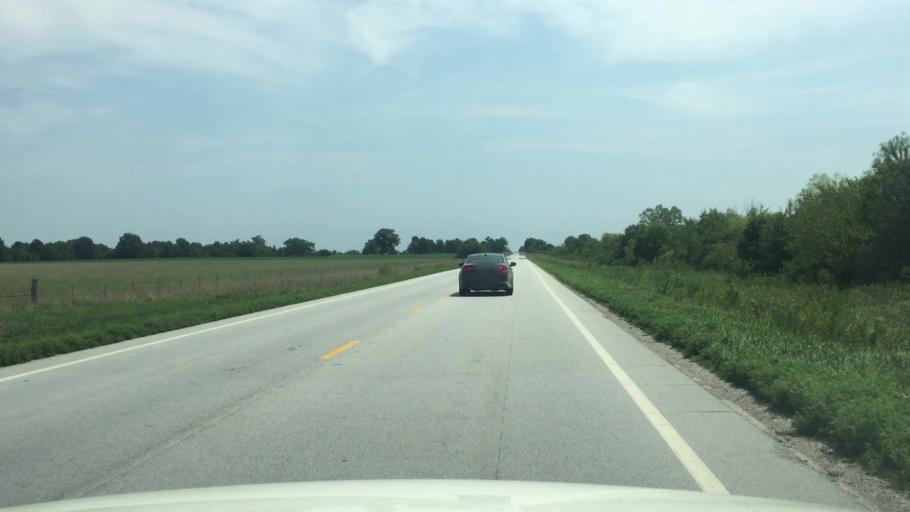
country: US
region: Kansas
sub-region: Cherokee County
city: Columbus
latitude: 37.1790
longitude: -94.9001
